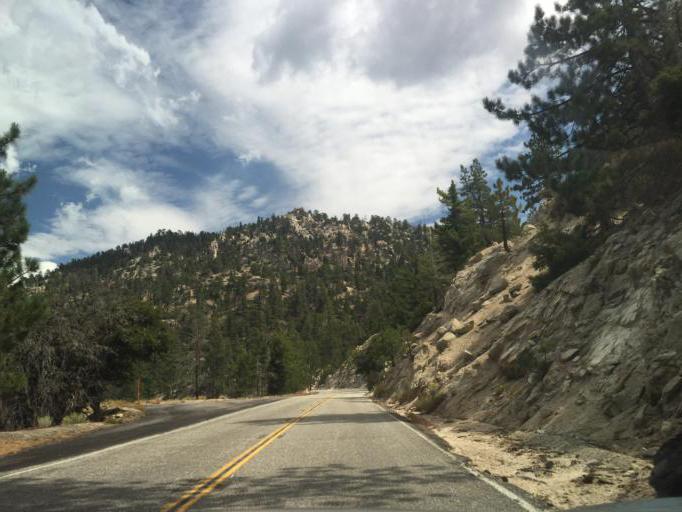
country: US
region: California
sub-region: Los Angeles County
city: Littlerock
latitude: 34.3430
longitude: -117.9768
